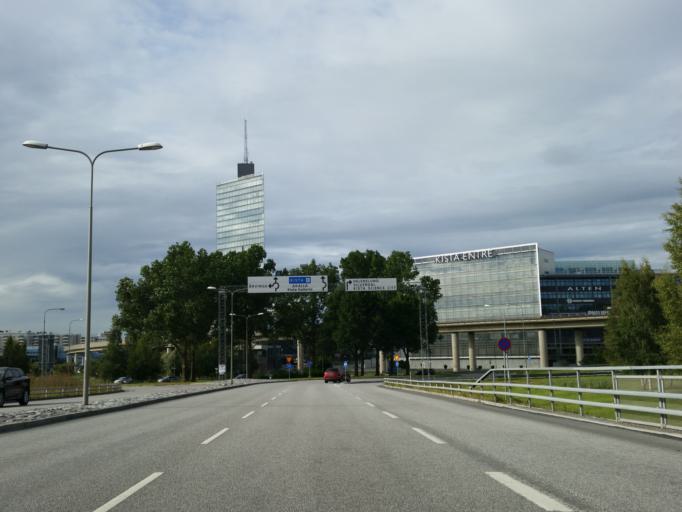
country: SE
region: Stockholm
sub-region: Stockholms Kommun
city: Kista
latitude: 59.3981
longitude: 17.9516
